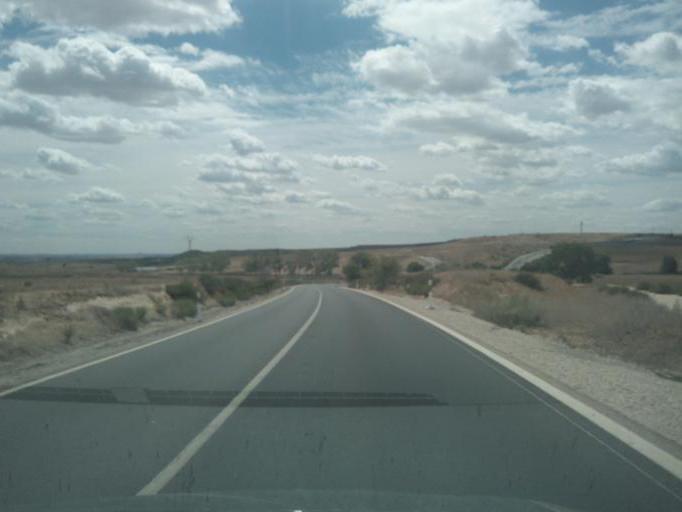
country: ES
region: Madrid
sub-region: Provincia de Madrid
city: Ajalvir
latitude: 40.5226
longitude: -3.4949
